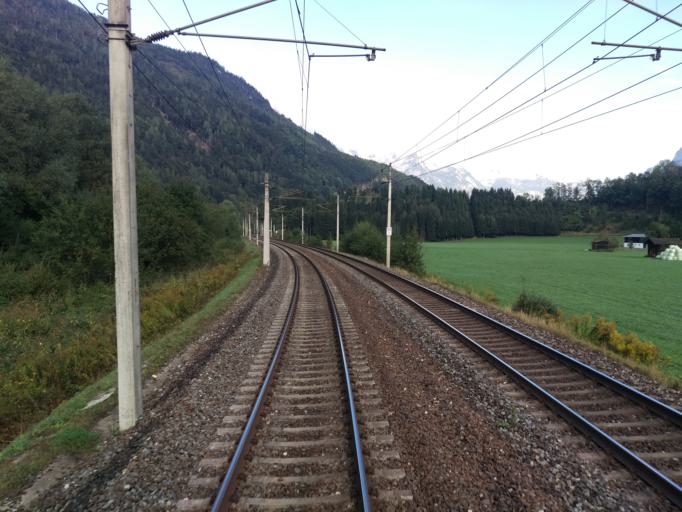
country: AT
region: Salzburg
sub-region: Politischer Bezirk Sankt Johann im Pongau
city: Bischofshofen
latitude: 47.4307
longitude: 13.2186
